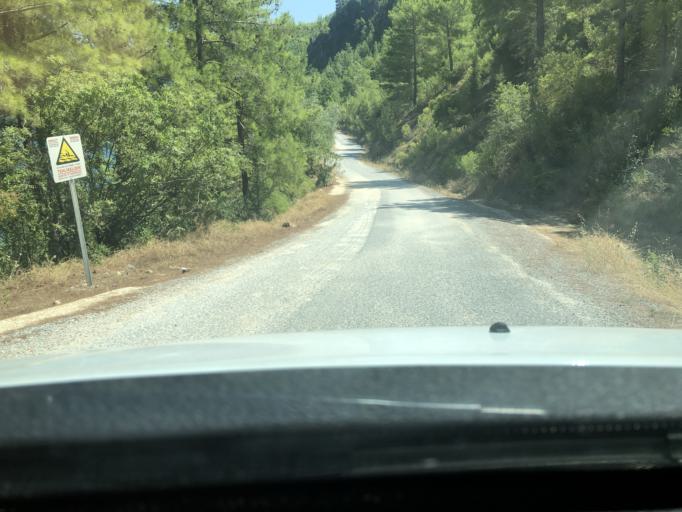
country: TR
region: Antalya
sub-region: Manavgat
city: Manavgat
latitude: 36.9106
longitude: 31.5503
